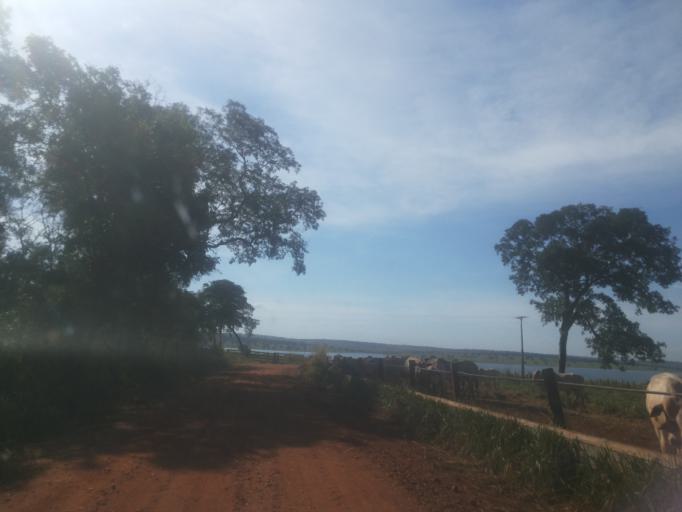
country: BR
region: Minas Gerais
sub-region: Santa Vitoria
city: Santa Vitoria
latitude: -19.0070
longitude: -50.4018
